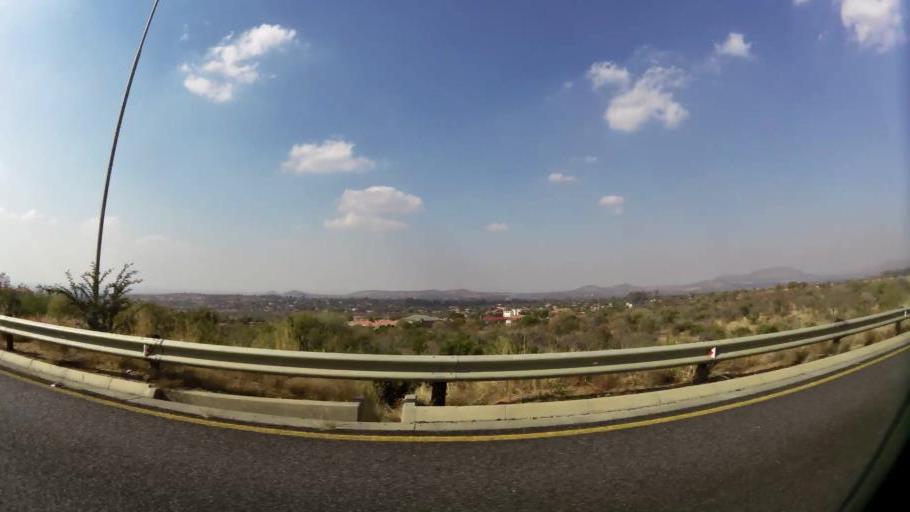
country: ZA
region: North-West
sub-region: Bojanala Platinum District Municipality
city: Rustenburg
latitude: -25.5905
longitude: 27.1275
